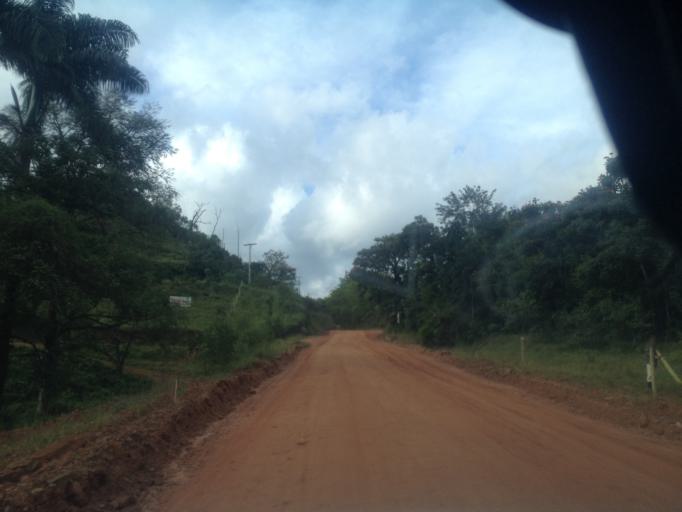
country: BR
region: Rio de Janeiro
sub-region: Quatis
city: Quatis
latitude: -22.2158
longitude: -44.2476
